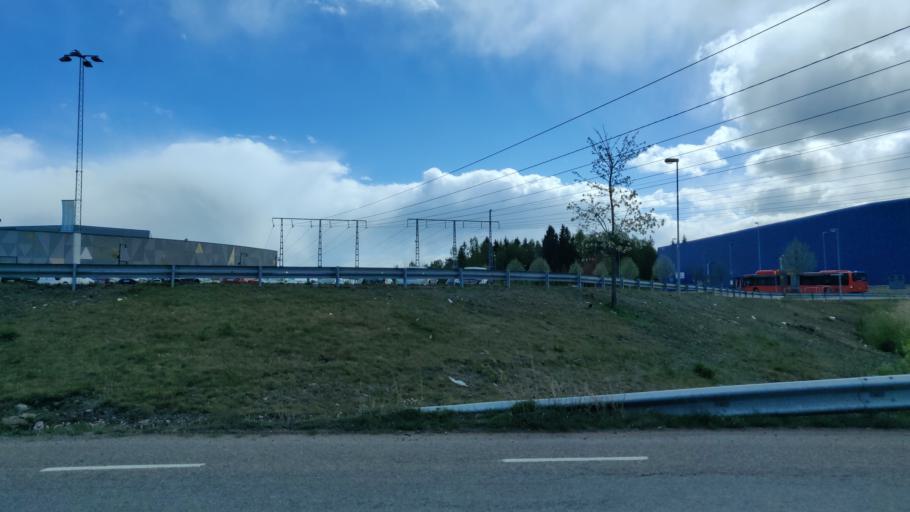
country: SE
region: Vaermland
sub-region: Hammaro Kommun
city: Skoghall
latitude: 59.3798
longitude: 13.4230
